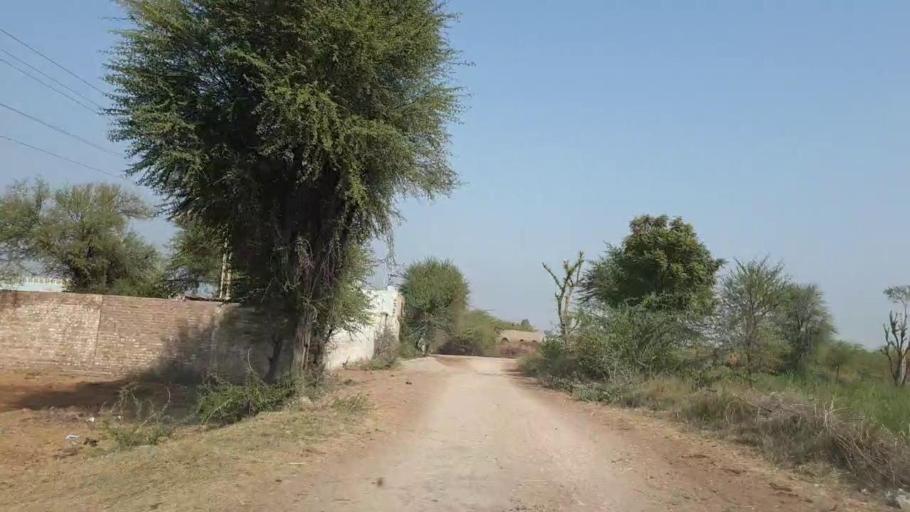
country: PK
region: Sindh
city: Mirpur Khas
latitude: 25.5860
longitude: 69.0124
